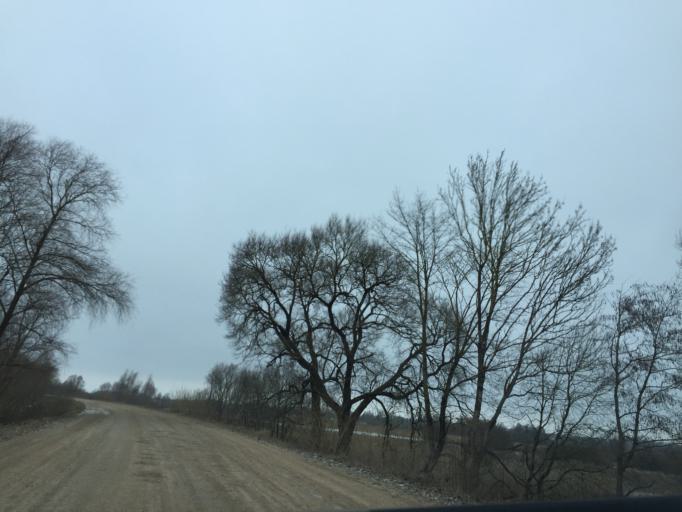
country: LV
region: Ozolnieku
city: Ozolnieki
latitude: 56.6353
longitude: 23.7999
